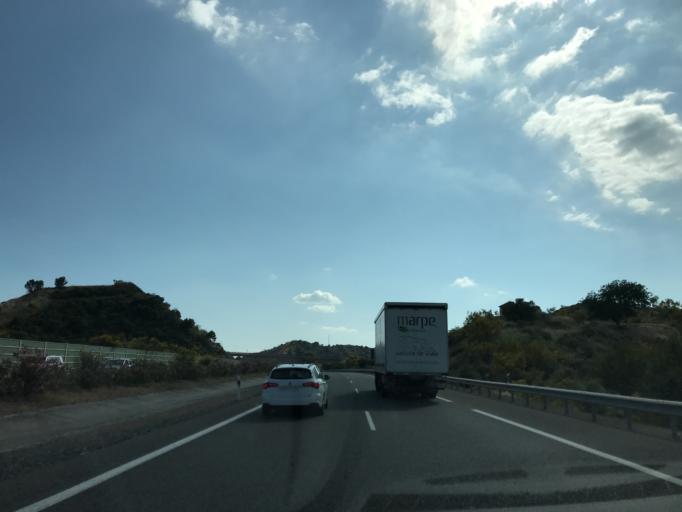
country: ES
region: Andalusia
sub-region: Provincia de Malaga
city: Istan
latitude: 36.5257
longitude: -4.9728
